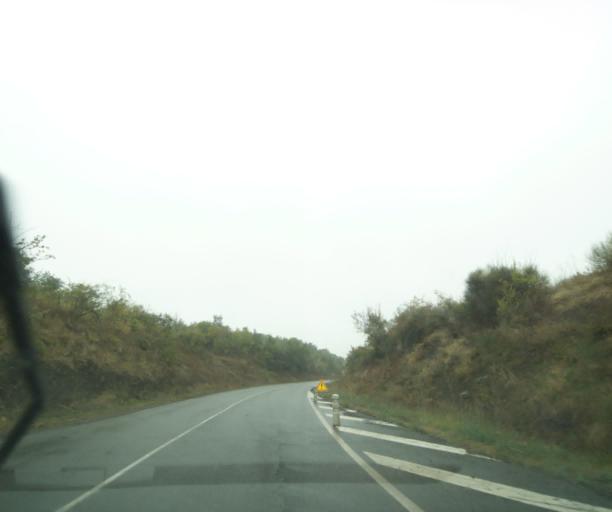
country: FR
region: Auvergne
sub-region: Departement du Puy-de-Dome
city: Blanzat
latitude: 45.8421
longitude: 3.0832
